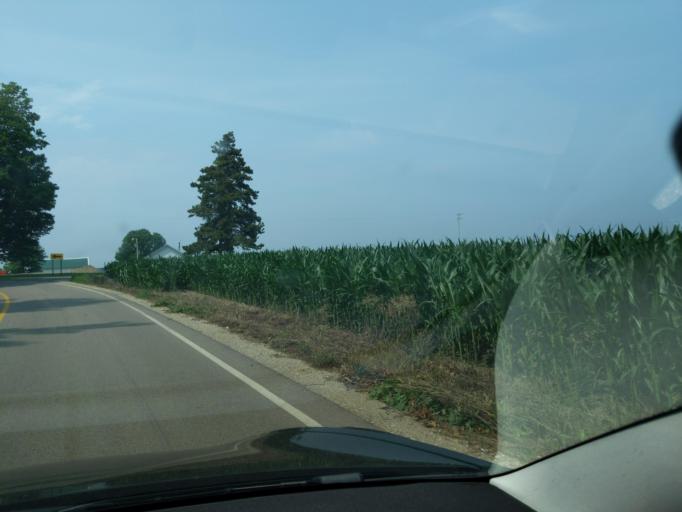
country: US
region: Michigan
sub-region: Clinton County
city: DeWitt
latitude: 42.9140
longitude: -84.5773
